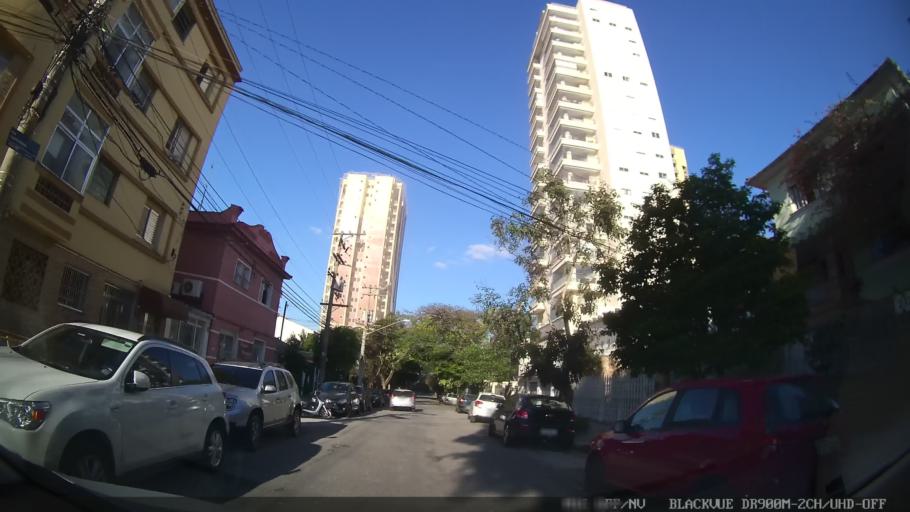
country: BR
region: Sao Paulo
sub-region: Sao Paulo
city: Sao Paulo
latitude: -23.4935
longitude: -46.6209
